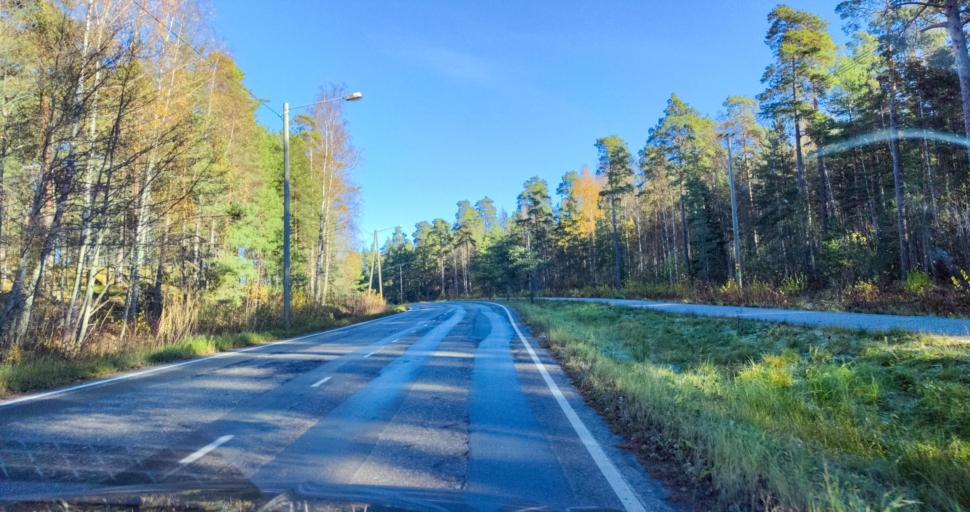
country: FI
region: Varsinais-Suomi
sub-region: Turku
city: Turku
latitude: 60.4214
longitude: 22.2158
